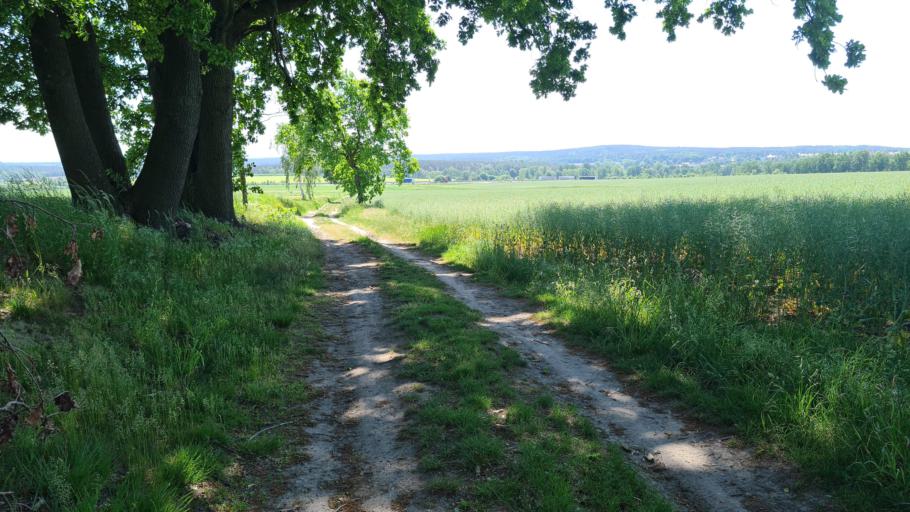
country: DE
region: Brandenburg
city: Grosskmehlen
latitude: 51.3614
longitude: 13.7233
